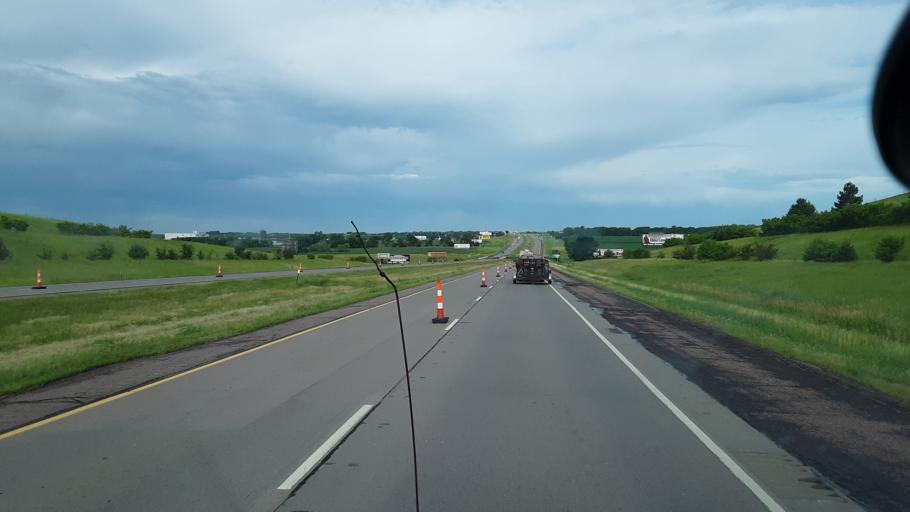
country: US
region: South Dakota
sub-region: Minnehaha County
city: Hartford
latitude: 43.6087
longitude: -96.8728
